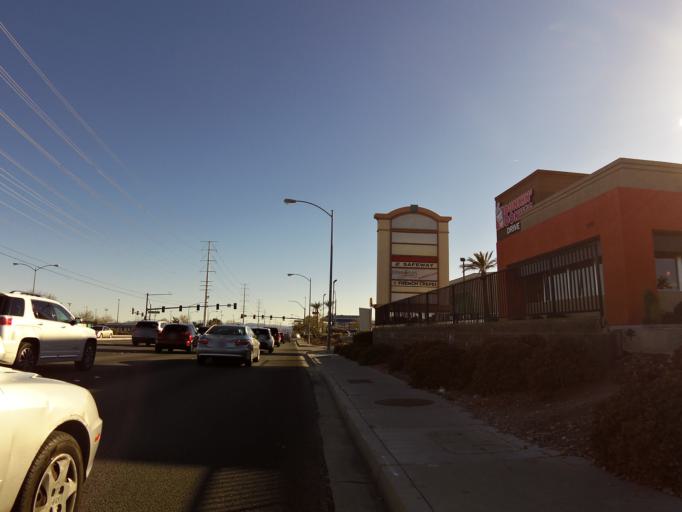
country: US
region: Nevada
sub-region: Clark County
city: Spring Valley
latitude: 36.1271
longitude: -115.2792
